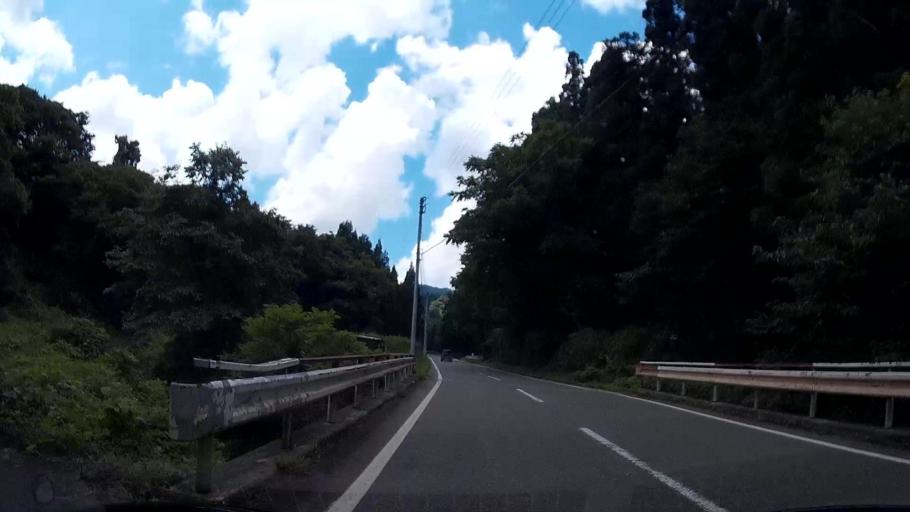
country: JP
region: Niigata
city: Shiozawa
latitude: 37.0197
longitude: 138.8170
